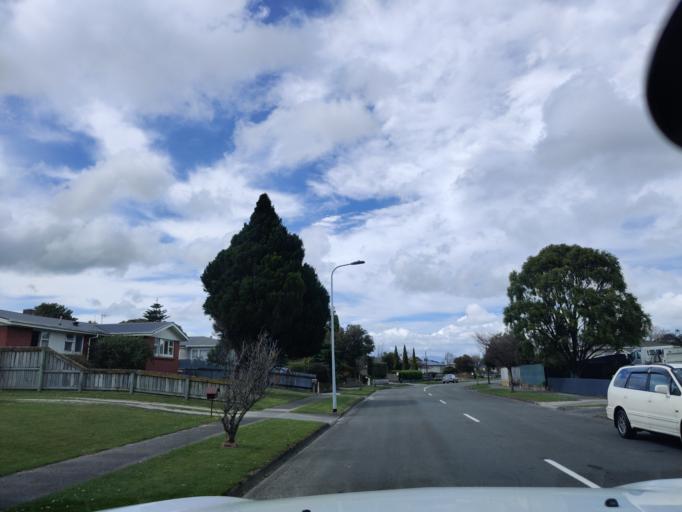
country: NZ
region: Manawatu-Wanganui
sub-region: Palmerston North City
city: Palmerston North
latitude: -40.3609
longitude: 175.5810
